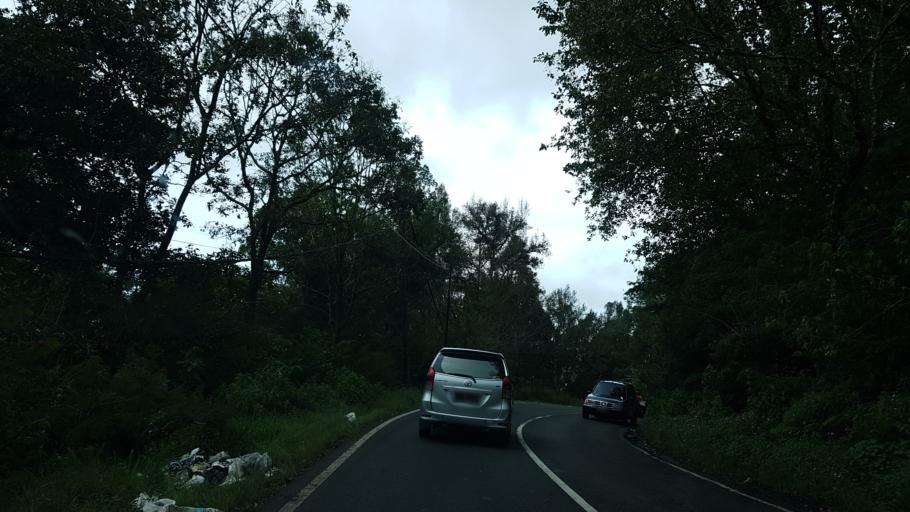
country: ID
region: West Java
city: Banjar
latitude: -7.1352
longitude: 107.4072
